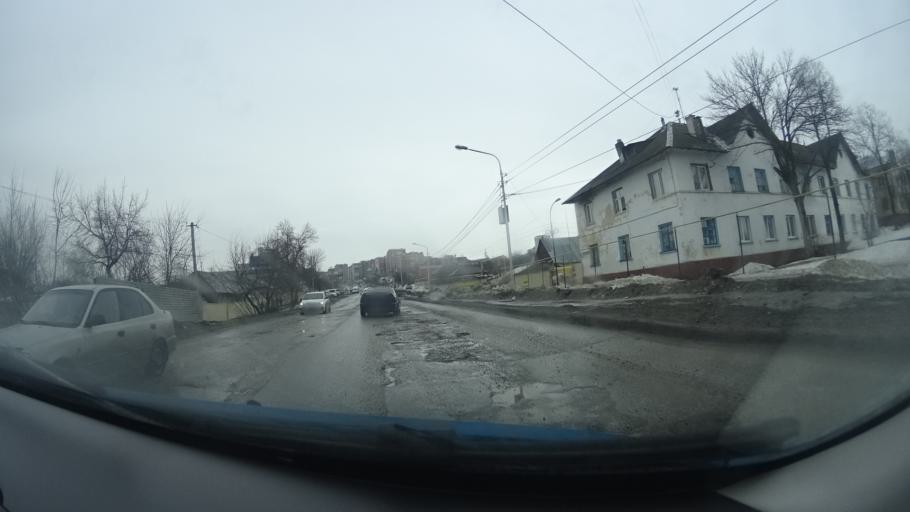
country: RU
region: Bashkortostan
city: Ufa
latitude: 54.7109
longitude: 55.9802
